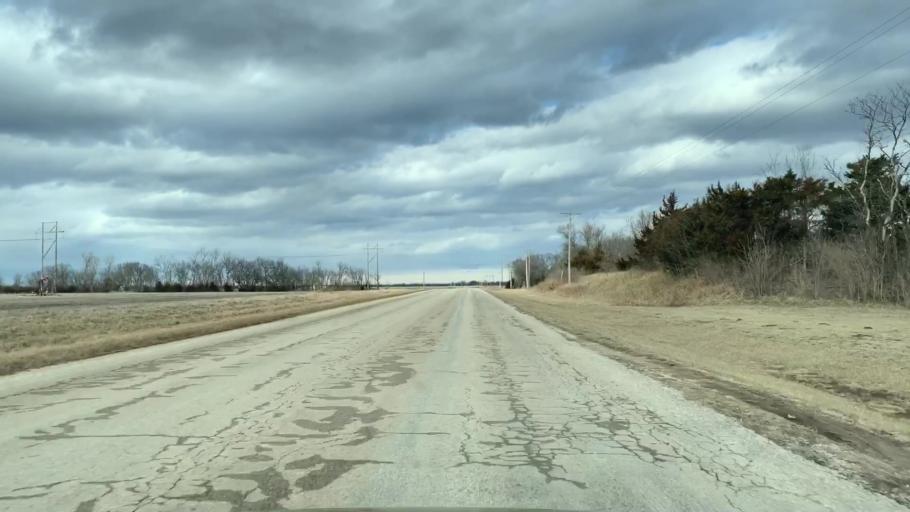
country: US
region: Kansas
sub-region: Allen County
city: Humboldt
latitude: 37.7661
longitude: -95.4706
